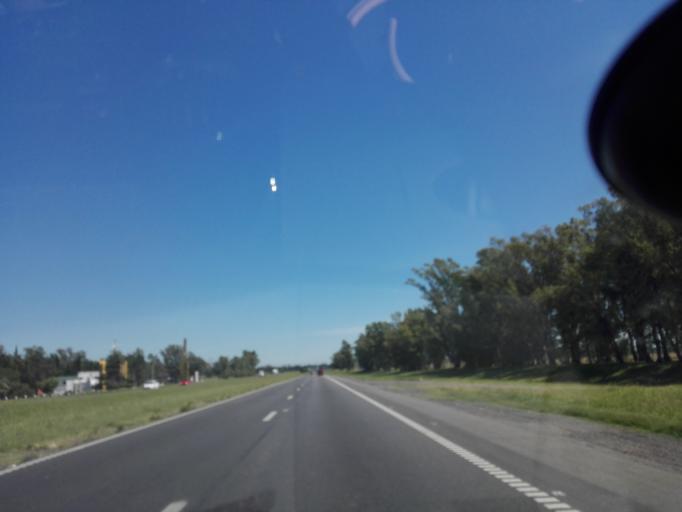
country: AR
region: Buenos Aires
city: San Nicolas de los Arroyos
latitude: -33.4234
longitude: -60.1782
